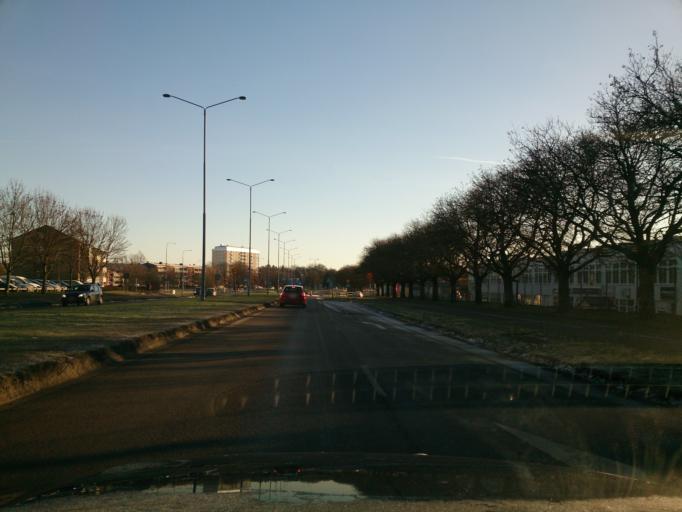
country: SE
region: OEstergoetland
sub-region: Norrkopings Kommun
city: Norrkoping
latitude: 58.5970
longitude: 16.1548
